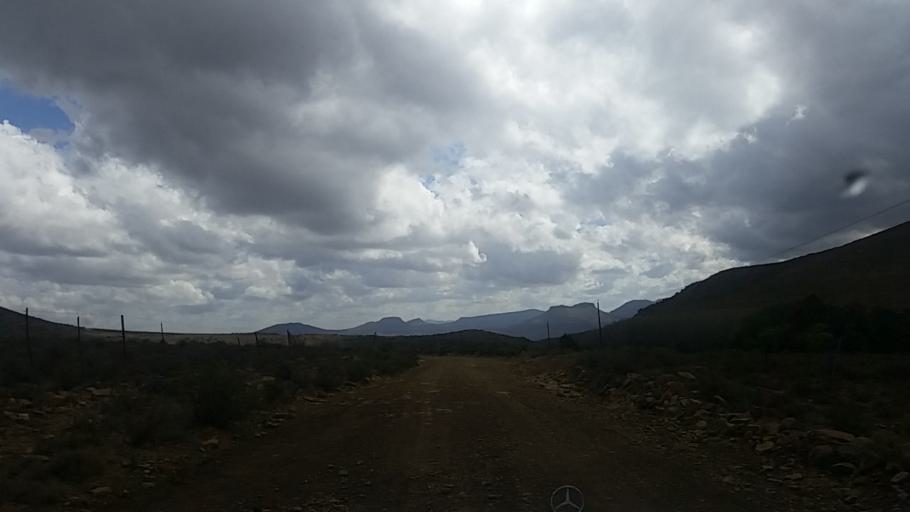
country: ZA
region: Eastern Cape
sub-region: Chris Hani District Municipality
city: Middelburg
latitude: -31.7903
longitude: 24.6650
